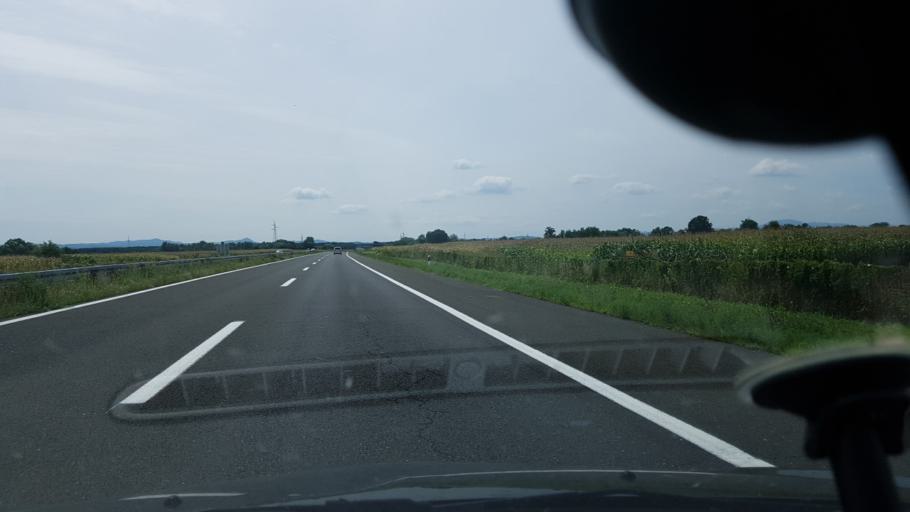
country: HR
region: Medimurska
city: Orehovica
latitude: 46.3330
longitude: 16.5243
